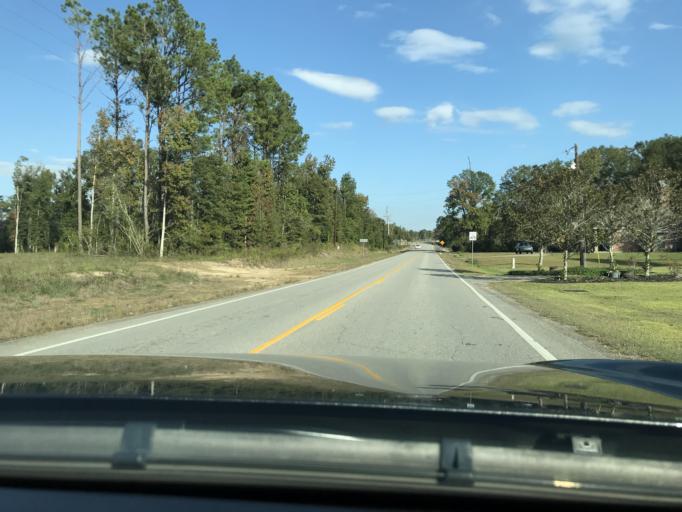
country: US
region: Louisiana
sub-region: Calcasieu Parish
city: Moss Bluff
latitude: 30.3394
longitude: -93.2578
